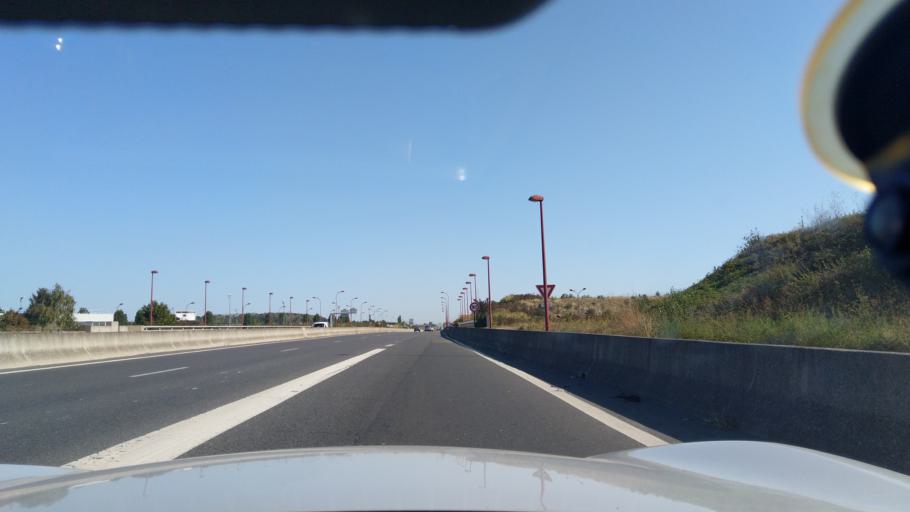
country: FR
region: Ile-de-France
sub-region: Departement du Val-d'Oise
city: Gonesse
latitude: 48.9770
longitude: 2.4638
